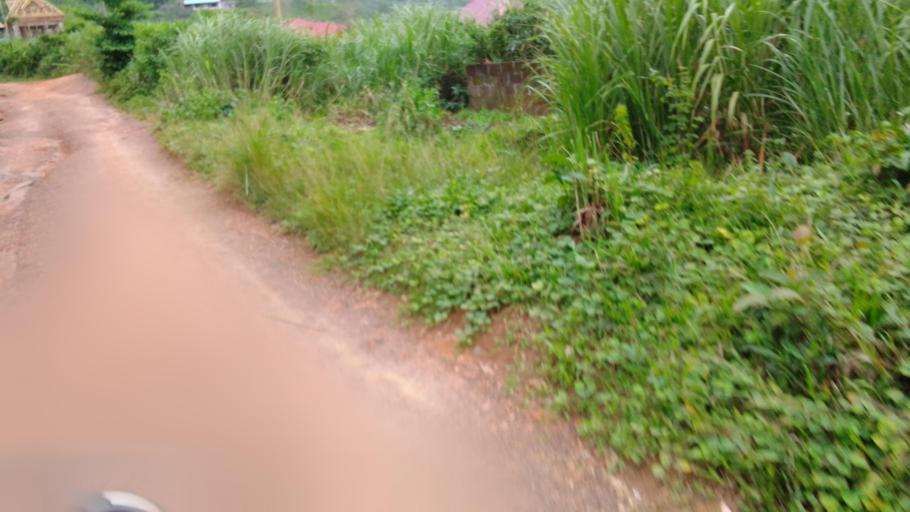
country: SL
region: Eastern Province
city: Kenema
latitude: 7.8902
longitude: -11.1946
